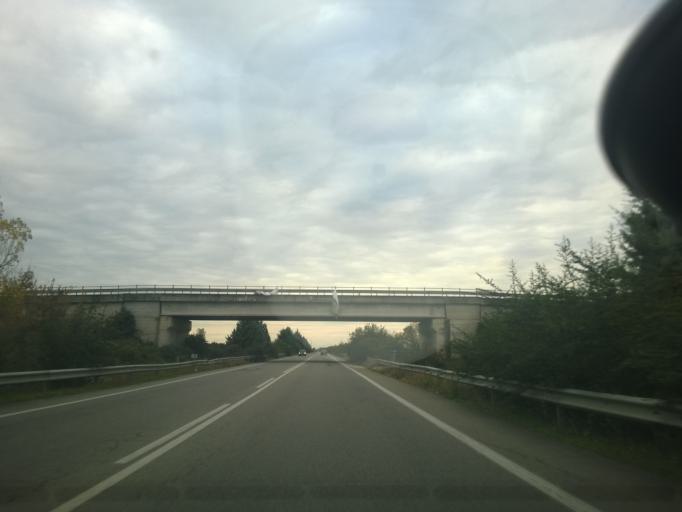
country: GR
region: Central Macedonia
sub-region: Nomos Pellis
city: Palaifyto
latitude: 40.7891
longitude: 22.2846
